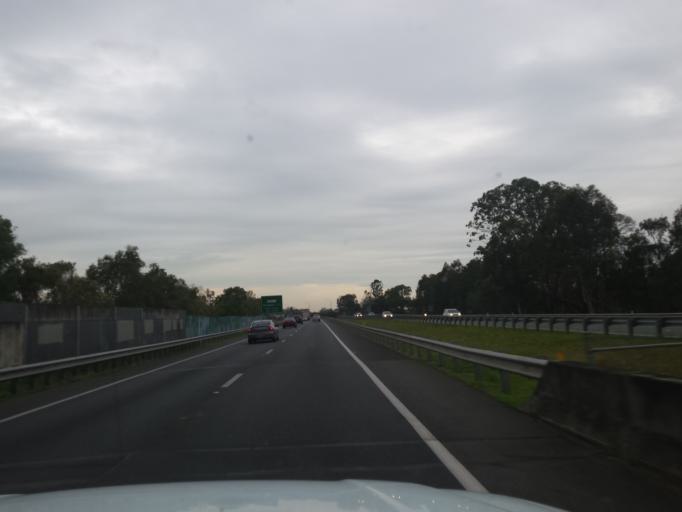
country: AU
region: Queensland
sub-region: Logan
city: Slacks Creek
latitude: -27.6802
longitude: 153.1702
